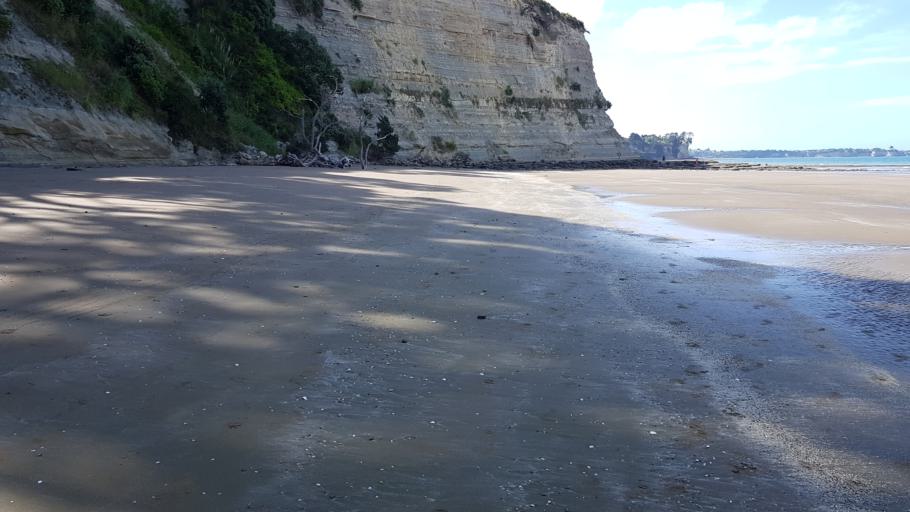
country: NZ
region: Auckland
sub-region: Auckland
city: Rothesay Bay
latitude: -36.6784
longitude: 174.7485
